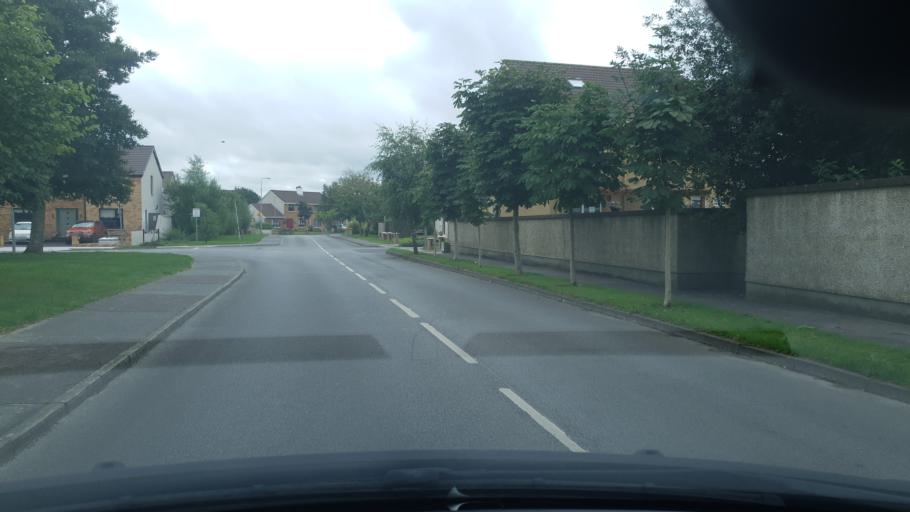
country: IE
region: Munster
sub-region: Ciarrai
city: Tralee
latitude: 52.2589
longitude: -9.6841
